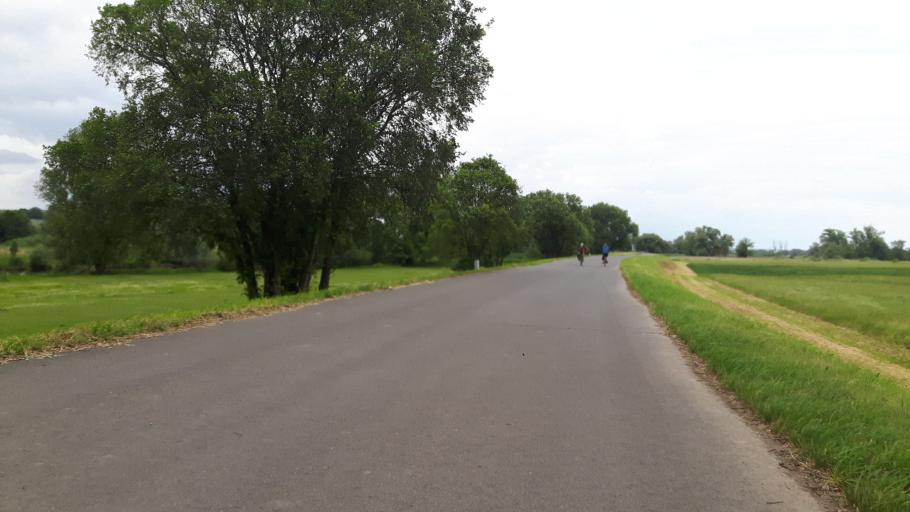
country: DE
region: Brandenburg
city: Schoneberg
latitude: 52.9254
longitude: 14.1280
